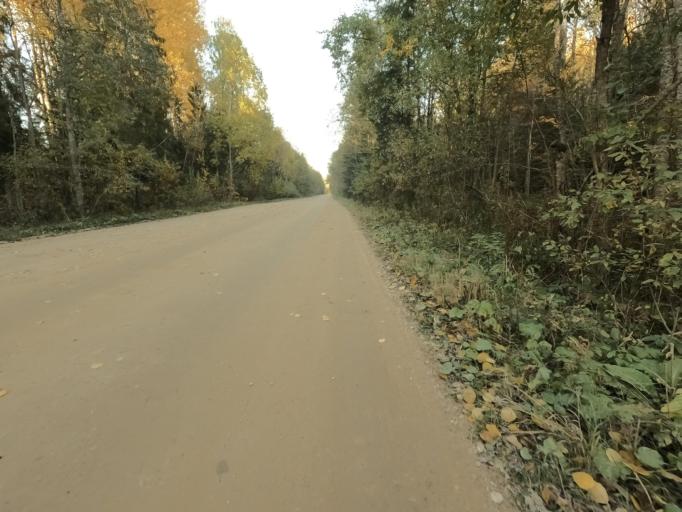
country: RU
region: Leningrad
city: Lyuban'
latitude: 58.9876
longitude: 31.1008
